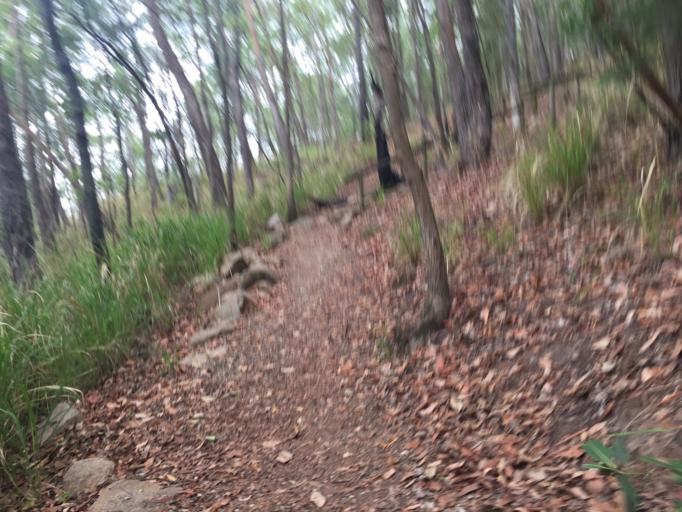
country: AU
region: Queensland
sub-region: Brisbane
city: Taringa
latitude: -27.4546
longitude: 152.9580
